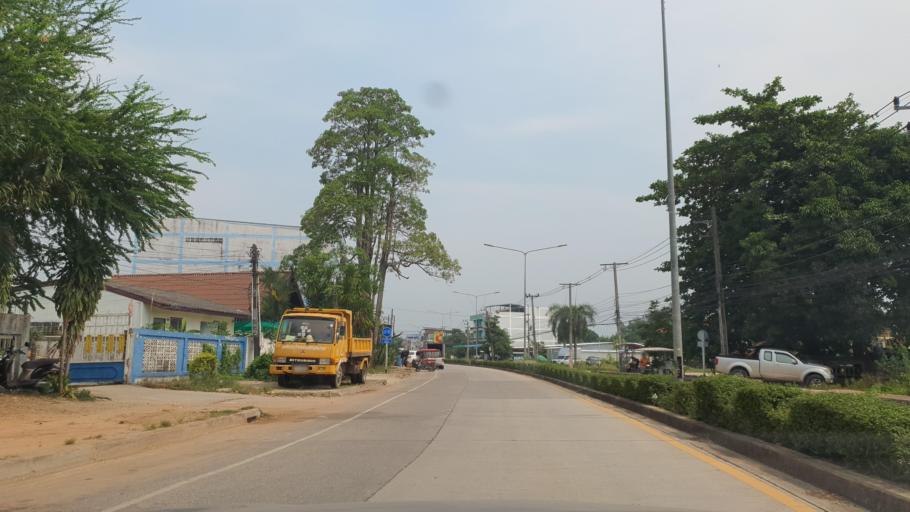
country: TH
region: Rayong
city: Rayong
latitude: 12.6267
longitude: 101.4235
